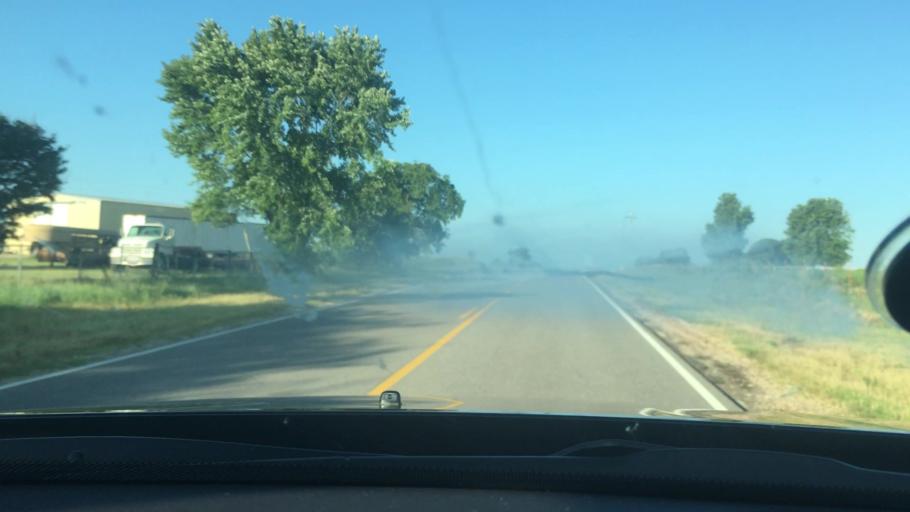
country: US
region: Oklahoma
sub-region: Pontotoc County
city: Ada
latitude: 34.6450
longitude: -96.8032
